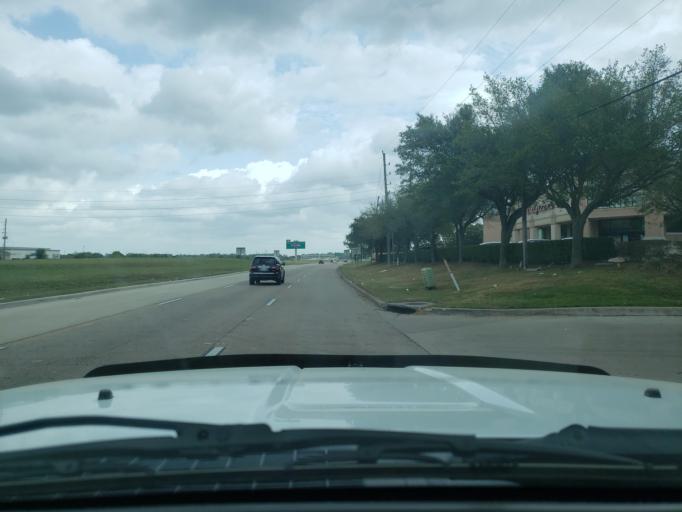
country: US
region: Texas
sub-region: Fort Bend County
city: Greatwood
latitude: 29.5650
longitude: -95.6874
